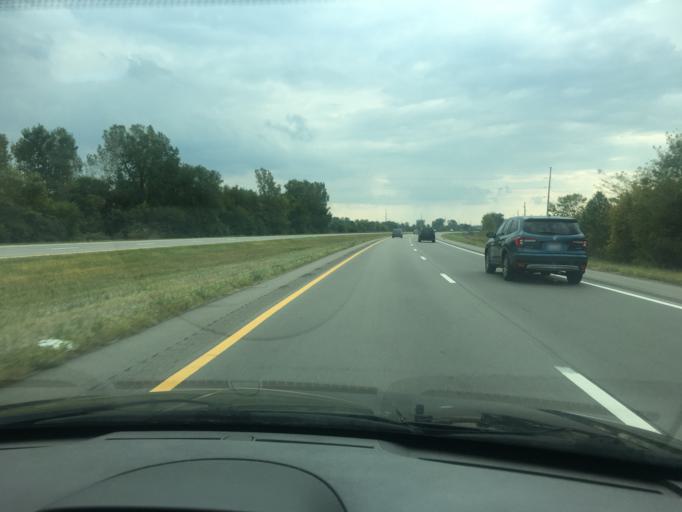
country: US
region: Ohio
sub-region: Clark County
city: Springfield
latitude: 39.9685
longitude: -83.8182
